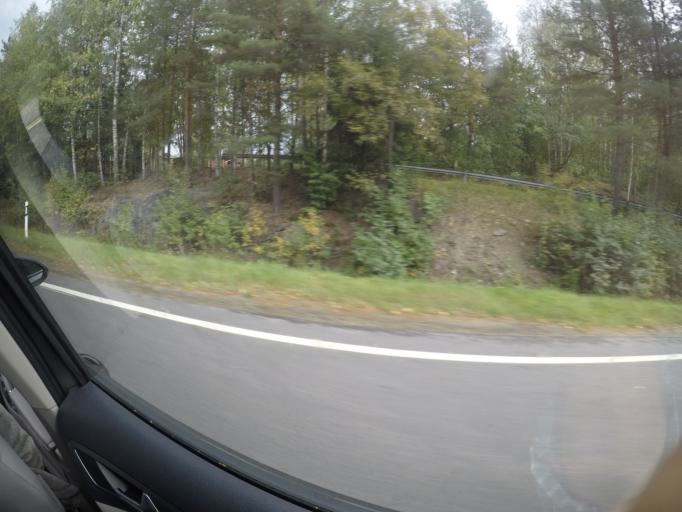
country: FI
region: Haeme
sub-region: Haemeenlinna
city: Parola
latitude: 61.0819
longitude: 24.3960
